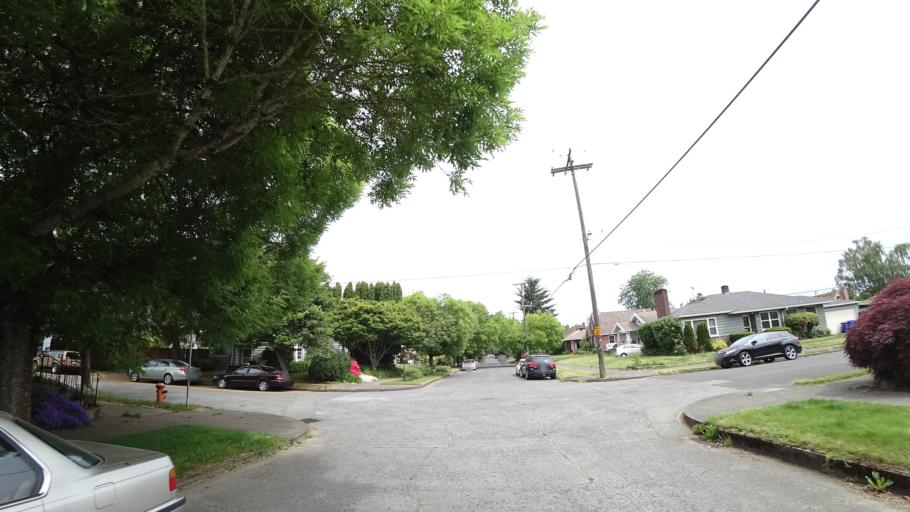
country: US
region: Oregon
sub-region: Multnomah County
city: Portland
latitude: 45.5703
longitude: -122.6435
